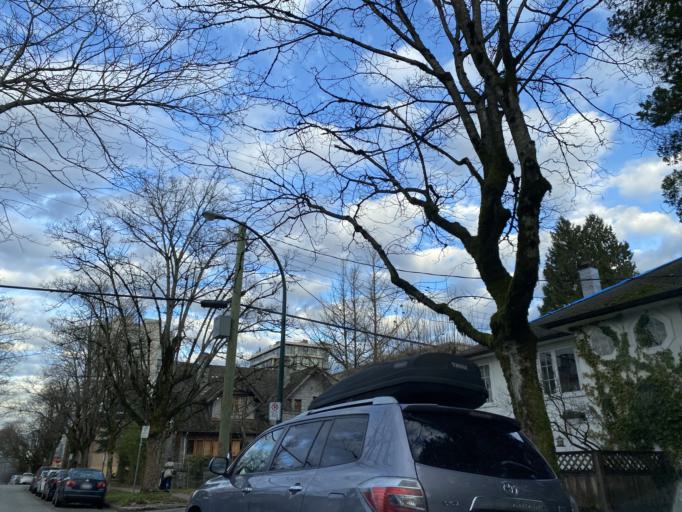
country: CA
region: British Columbia
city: Vancouver
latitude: 49.2618
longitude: -123.1291
